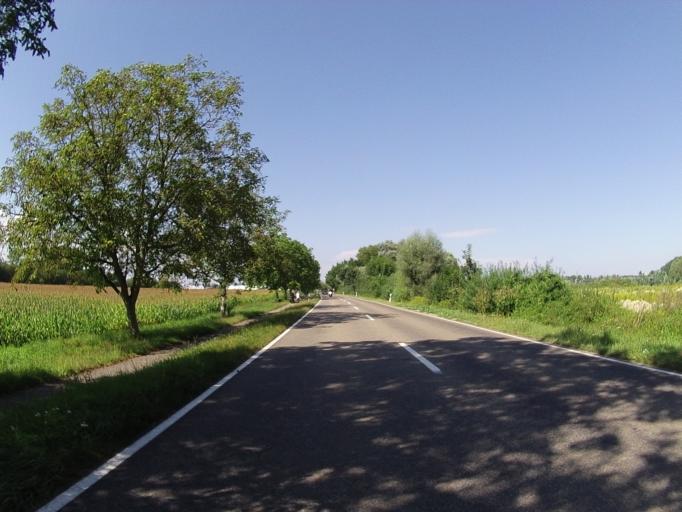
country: DE
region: Rheinland-Pfalz
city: Neuburg
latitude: 49.0001
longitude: 8.2598
